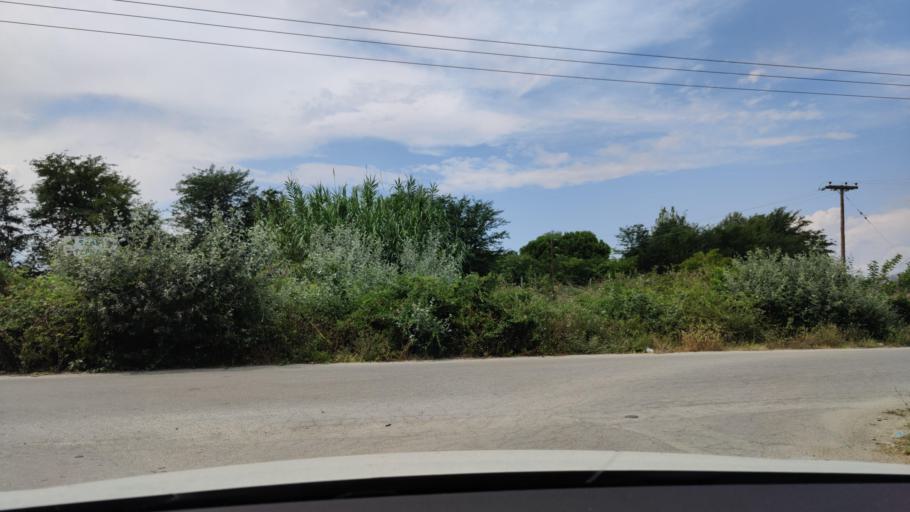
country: GR
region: Central Macedonia
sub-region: Nomos Serron
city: Serres
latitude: 41.0684
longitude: 23.5562
